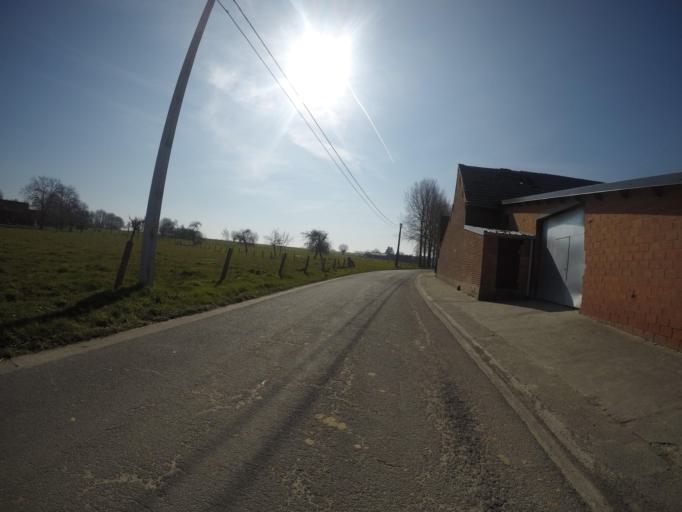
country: BE
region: Flanders
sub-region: Provincie Oost-Vlaanderen
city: Sint-Maria-Lierde
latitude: 50.7963
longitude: 3.8413
